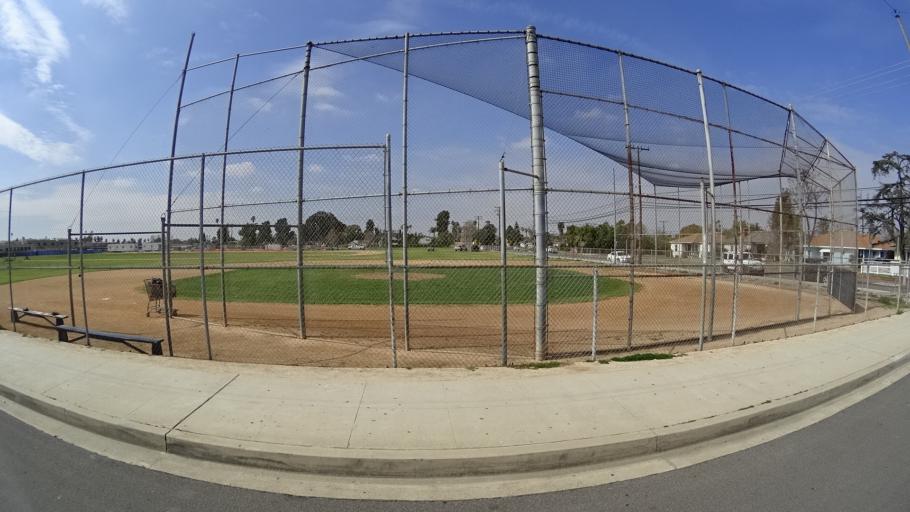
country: US
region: California
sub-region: Orange County
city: Anaheim
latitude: 33.8374
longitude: -117.9247
